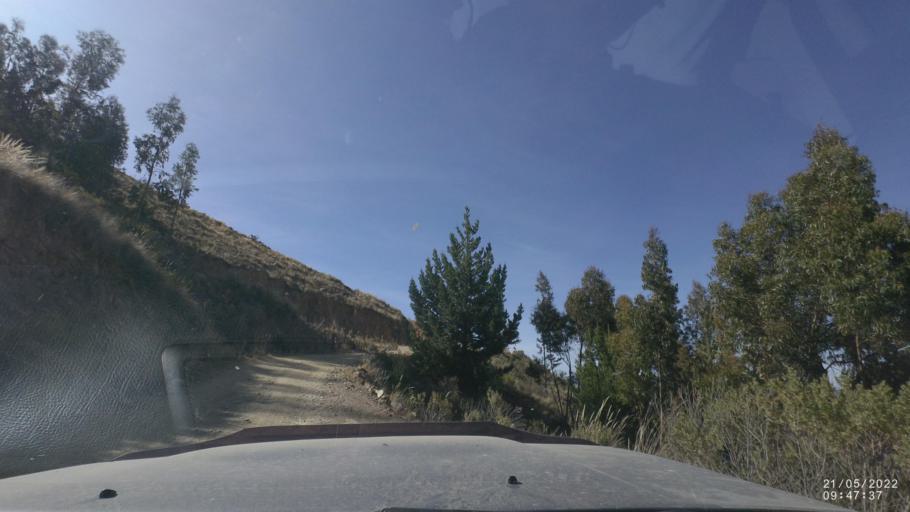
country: BO
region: Cochabamba
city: Colomi
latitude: -17.3431
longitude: -65.9980
